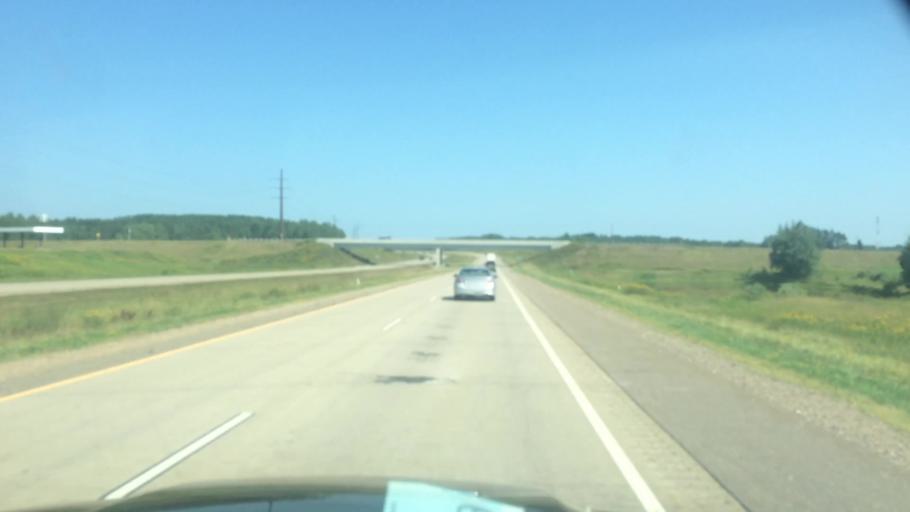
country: US
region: Wisconsin
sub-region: Lincoln County
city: Merrill
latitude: 45.2334
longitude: -89.6728
